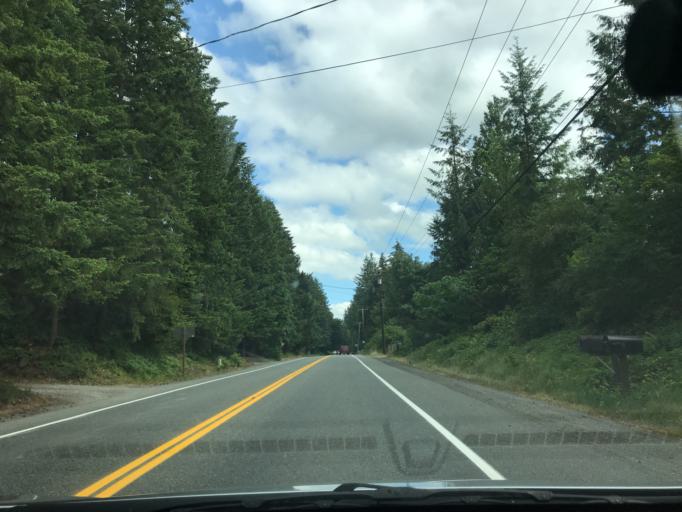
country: US
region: Washington
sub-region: King County
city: Lake Morton-Berrydale
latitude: 47.3116
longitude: -122.0940
